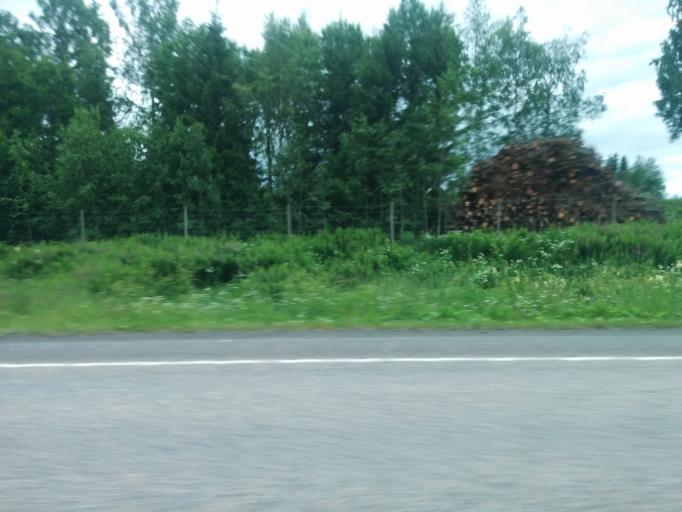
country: FI
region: Pirkanmaa
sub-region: Tampere
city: Orivesi
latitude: 61.7093
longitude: 24.4827
